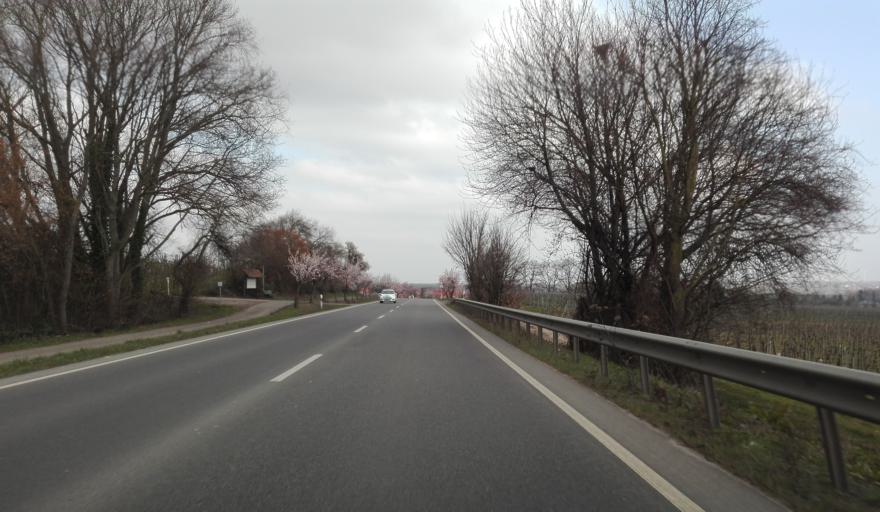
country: DE
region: Rheinland-Pfalz
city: Bockenheim
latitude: 49.5959
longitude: 8.1780
